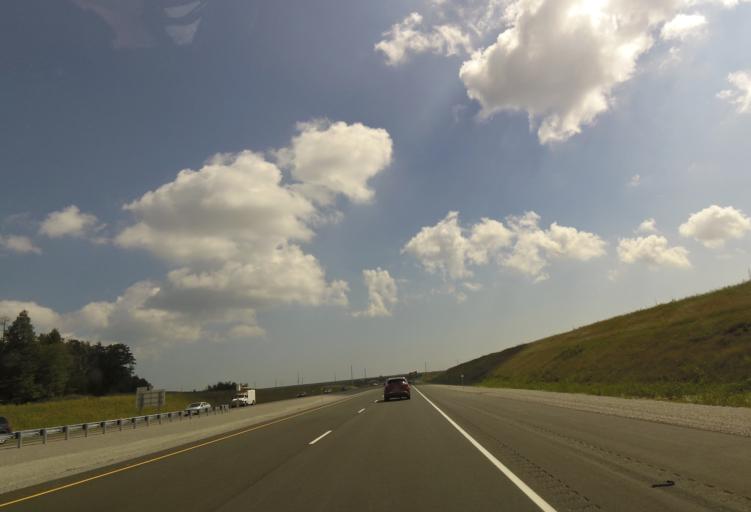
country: CA
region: Ontario
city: Ajax
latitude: 43.8938
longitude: -78.9915
